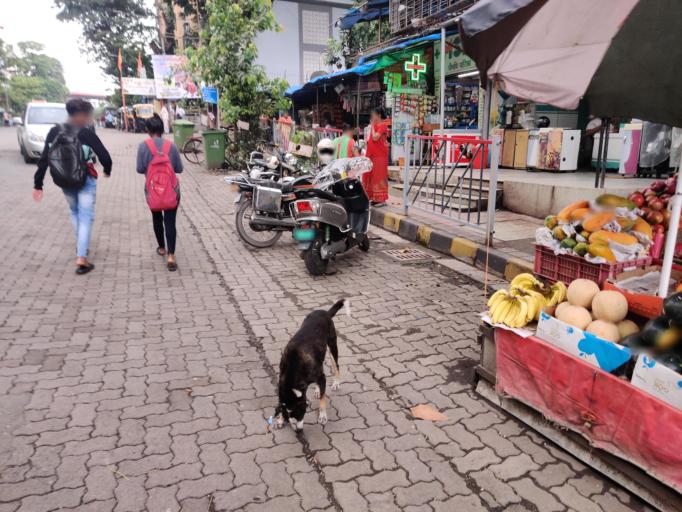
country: IN
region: Maharashtra
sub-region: Mumbai Suburban
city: Borivli
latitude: 19.2453
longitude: 72.8622
